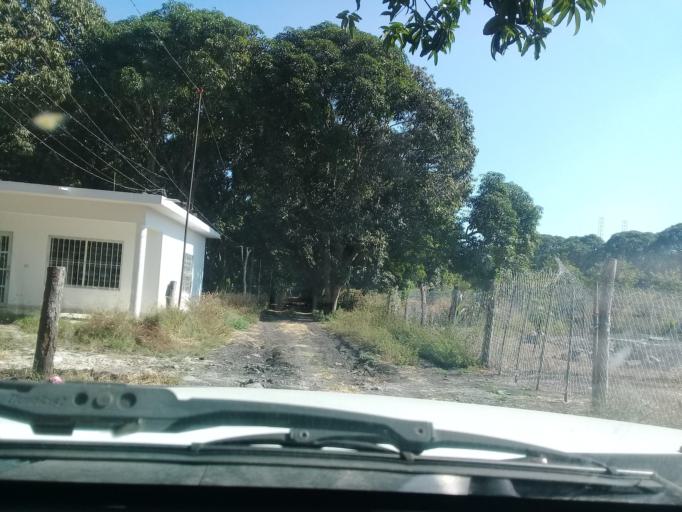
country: MX
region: Veracruz
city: Actopan
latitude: 19.4739
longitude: -96.5776
